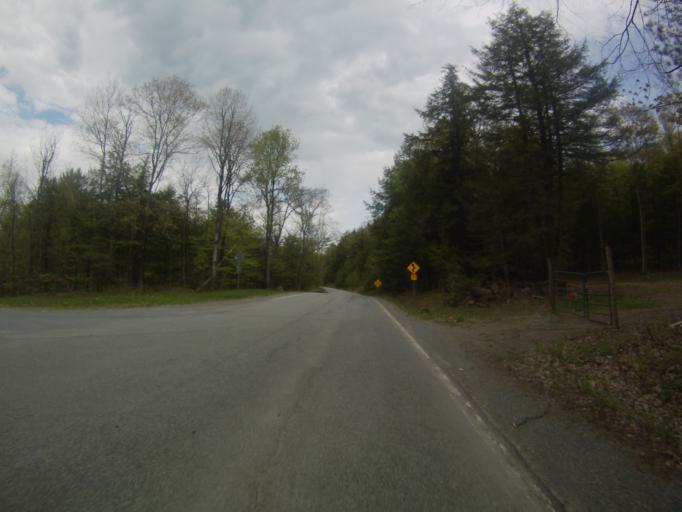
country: US
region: New York
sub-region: Essex County
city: Port Henry
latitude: 43.9440
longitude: -73.5015
